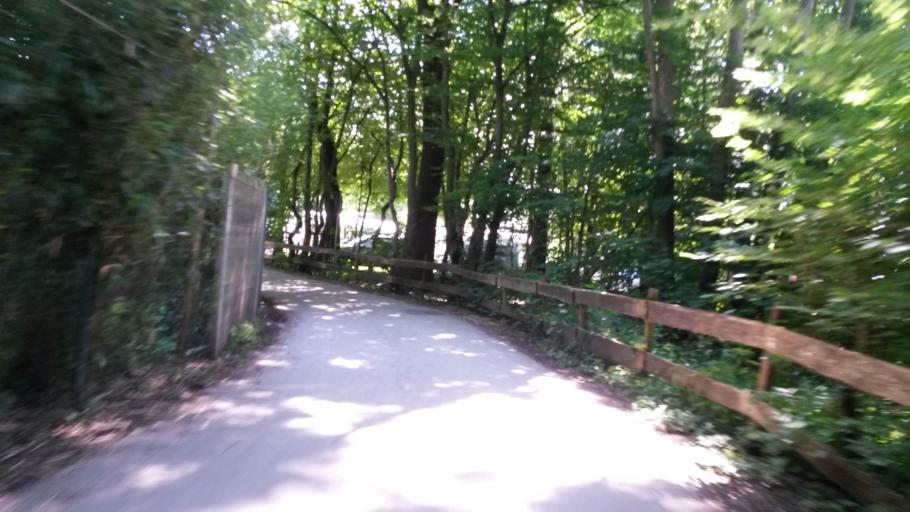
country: DE
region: Bavaria
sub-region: Upper Bavaria
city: Chieming
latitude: 47.9023
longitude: 12.5192
